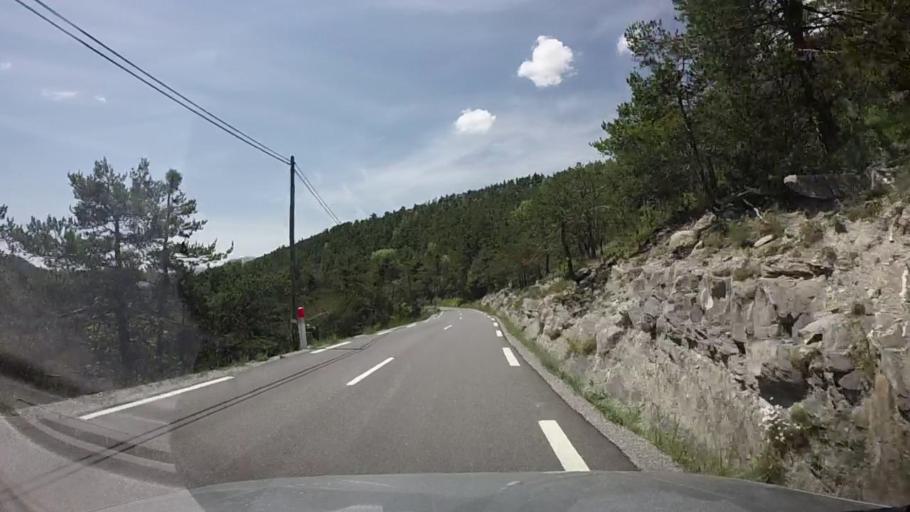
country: FR
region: Provence-Alpes-Cote d'Azur
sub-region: Departement des Alpes-de-Haute-Provence
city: Seyne-les-Alpes
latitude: 44.3949
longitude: 6.3338
